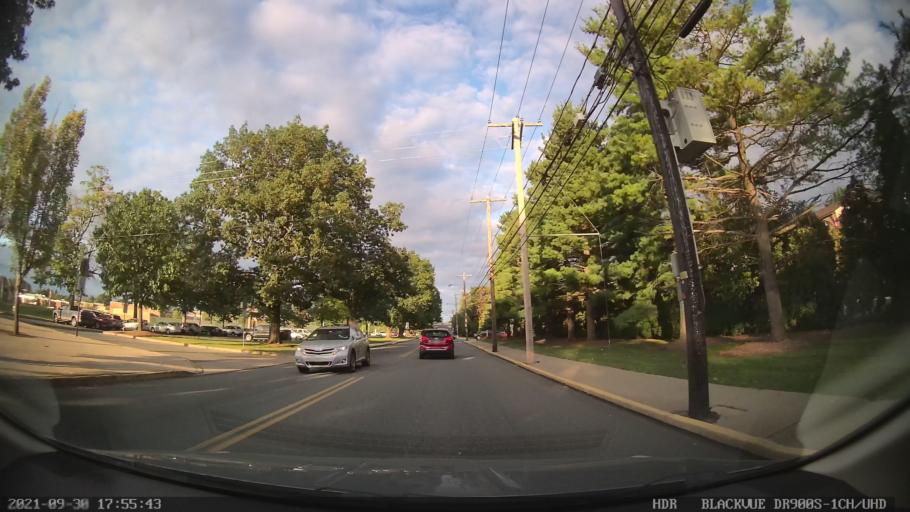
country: US
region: Pennsylvania
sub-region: Lehigh County
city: Emmaus
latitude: 40.5318
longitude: -75.5072
